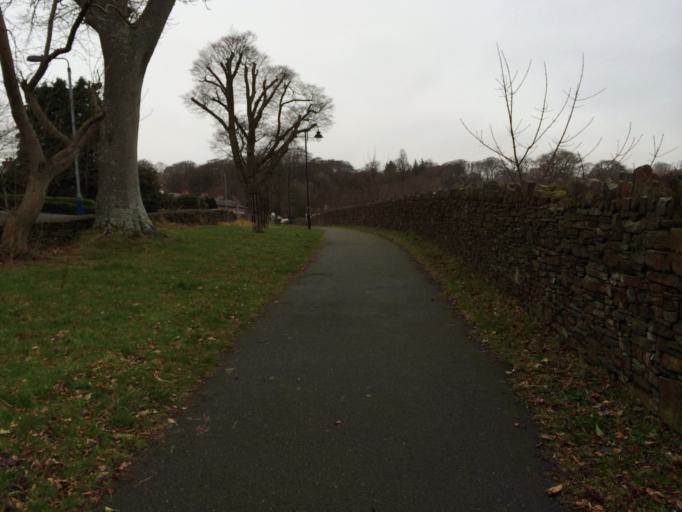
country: IM
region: Douglas
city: Douglas
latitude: 54.1554
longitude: -4.5065
